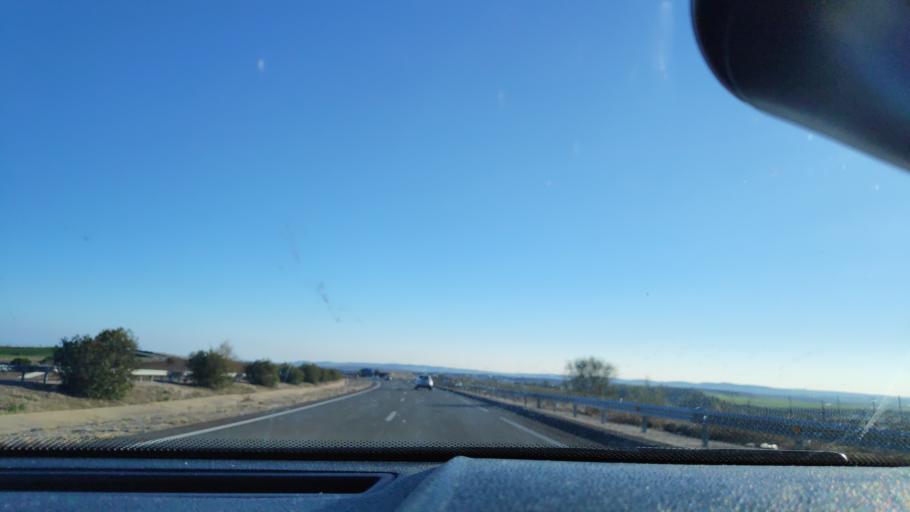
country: ES
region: Andalusia
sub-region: Provincia de Sevilla
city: Guillena
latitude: 37.5445
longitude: -6.1007
